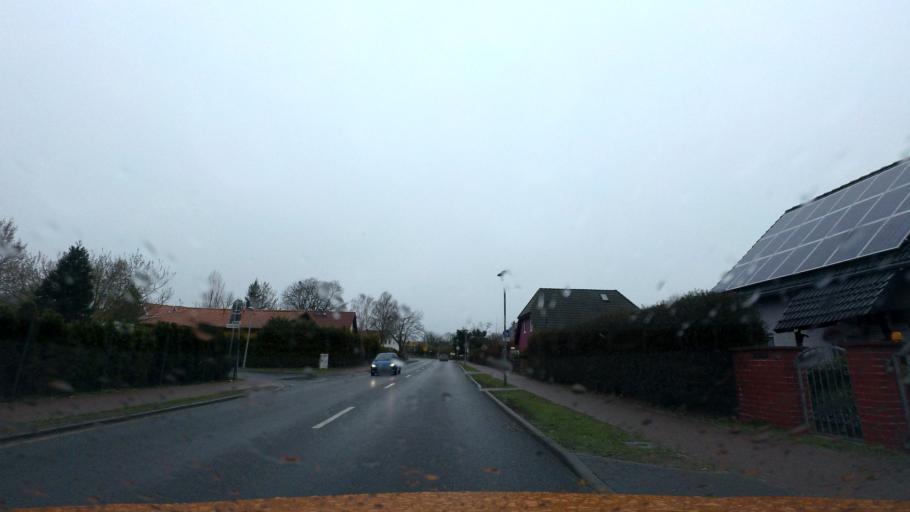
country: DE
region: Brandenburg
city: Velten
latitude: 52.6531
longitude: 13.1435
